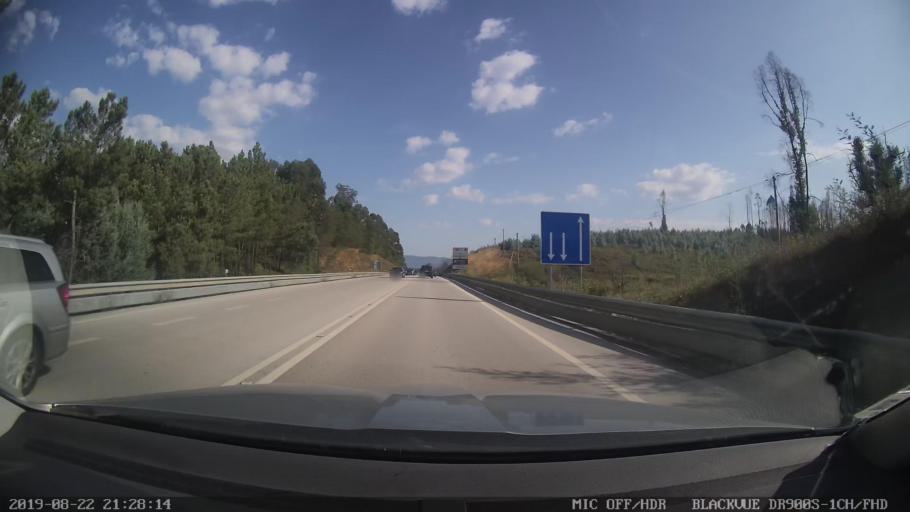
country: PT
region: Leiria
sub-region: Pedrogao Grande
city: Pedrogao Grande
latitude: 39.8897
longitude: -8.1209
